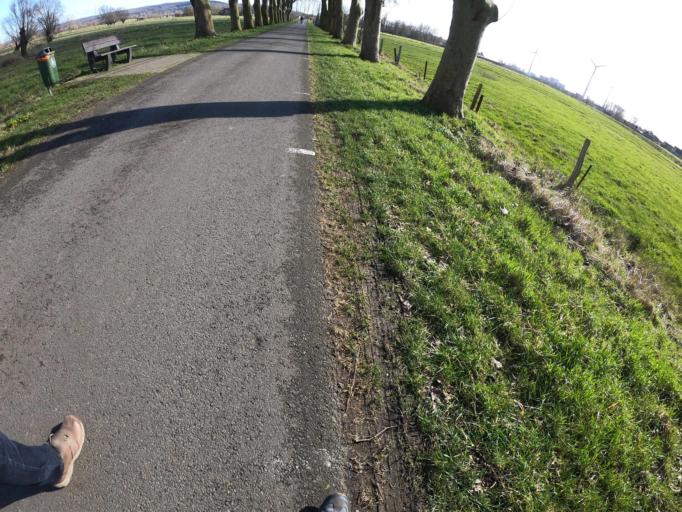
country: BE
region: Flanders
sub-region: Provincie West-Vlaanderen
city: Avelgem
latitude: 50.7742
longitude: 3.4503
